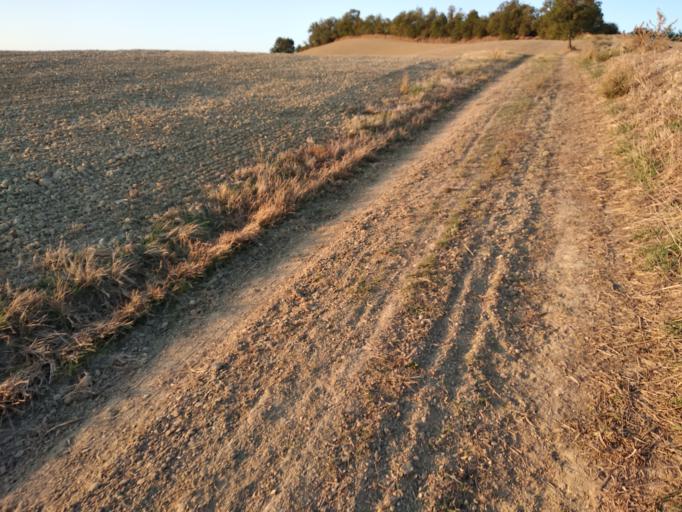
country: IT
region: Emilia-Romagna
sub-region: Provincia di Bologna
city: Dozza
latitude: 44.3394
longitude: 11.5986
